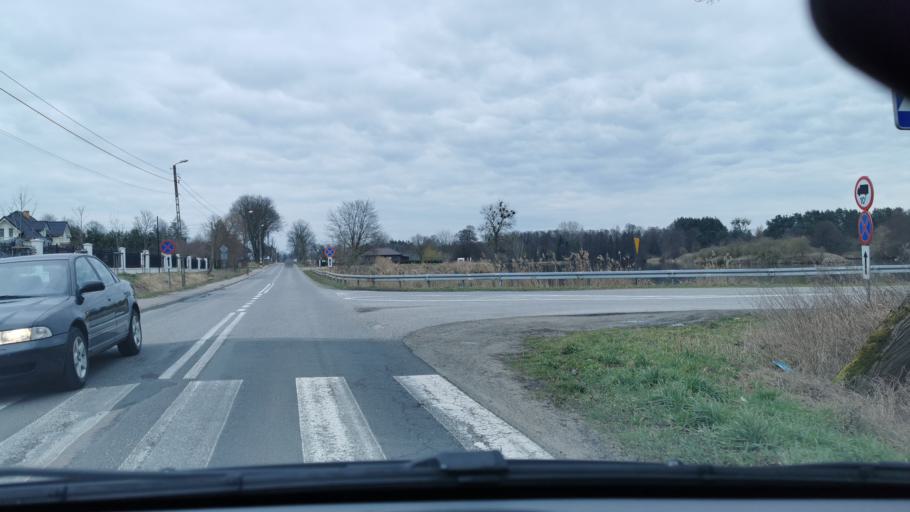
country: PL
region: Masovian Voivodeship
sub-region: Powiat zyrardowski
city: Radziejowice
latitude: 52.0118
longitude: 20.5210
